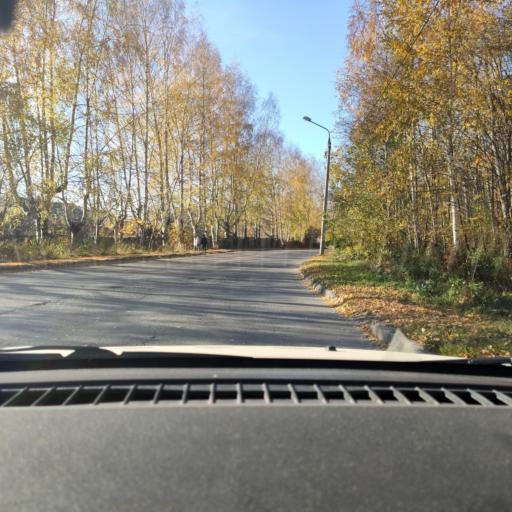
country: RU
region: Perm
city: Perm
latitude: 58.0795
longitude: 56.3695
